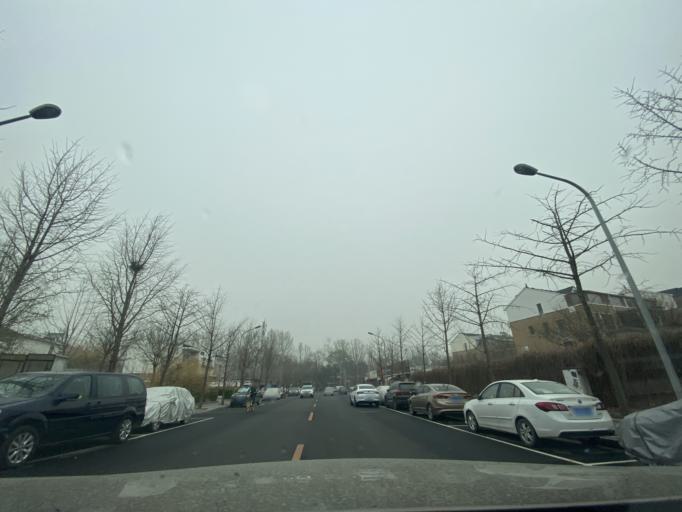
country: CN
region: Beijing
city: Sijiqing
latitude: 39.9574
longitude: 116.2285
